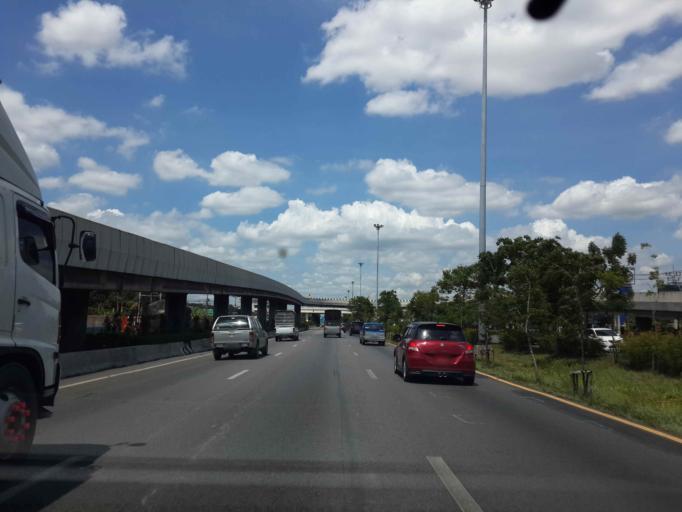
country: TH
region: Bangkok
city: Bang Bon
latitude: 13.6129
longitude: 100.3802
